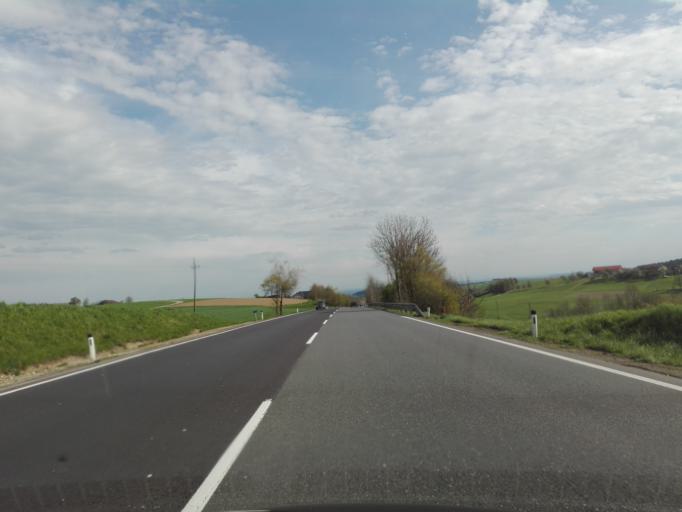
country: AT
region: Upper Austria
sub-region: Politischer Bezirk Urfahr-Umgebung
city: Herzogsdorf
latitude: 48.4143
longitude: 14.0636
